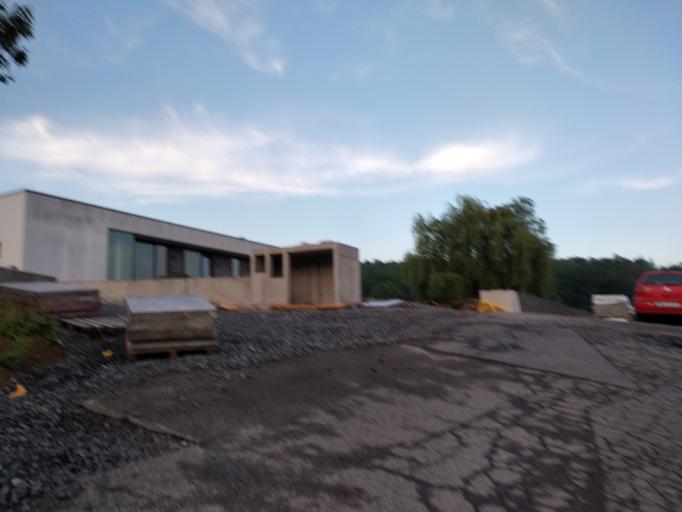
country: CZ
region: Moravskoslezsky
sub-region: Okres Frydek-Mistek
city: Frydek-Mistek
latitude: 49.6923
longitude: 18.3723
